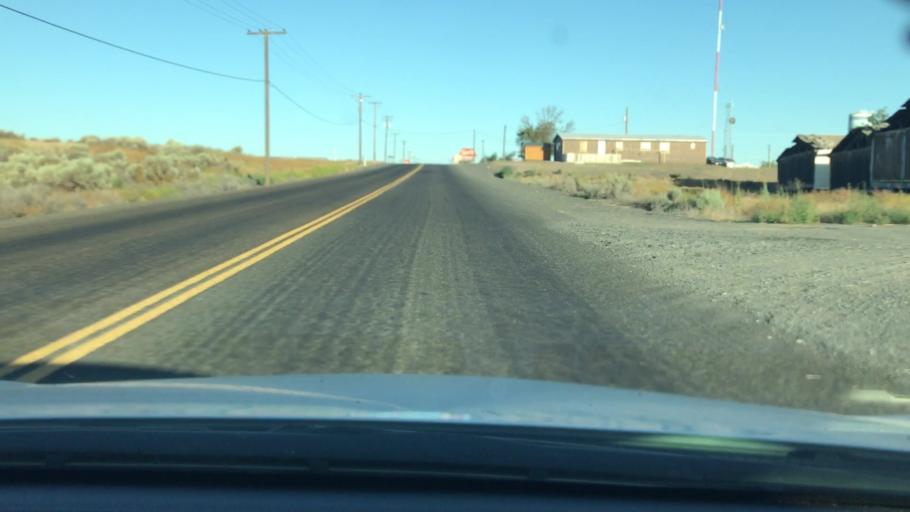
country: US
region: Washington
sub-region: Grant County
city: Moses Lake
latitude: 47.1017
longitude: -119.2386
